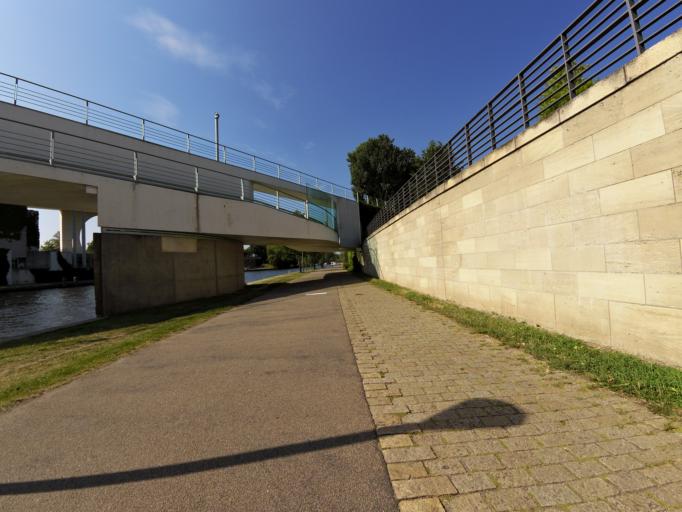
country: DE
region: Berlin
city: Tiergarten Bezirk
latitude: 52.5207
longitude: 13.3667
